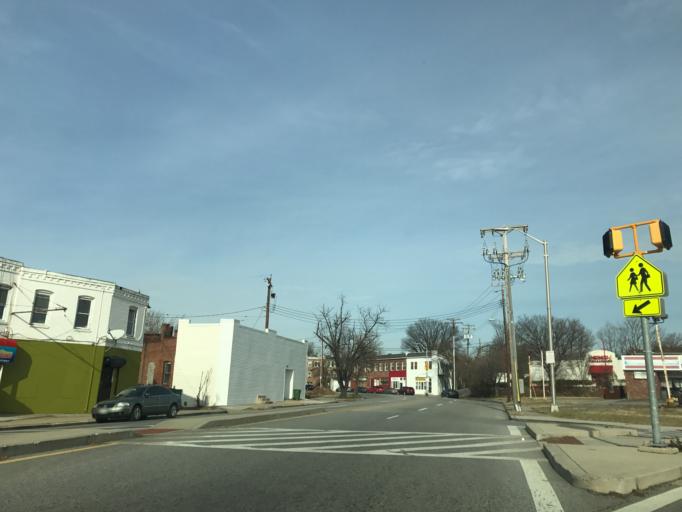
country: US
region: Maryland
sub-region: City of Baltimore
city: Baltimore
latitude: 39.3229
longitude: -76.5886
